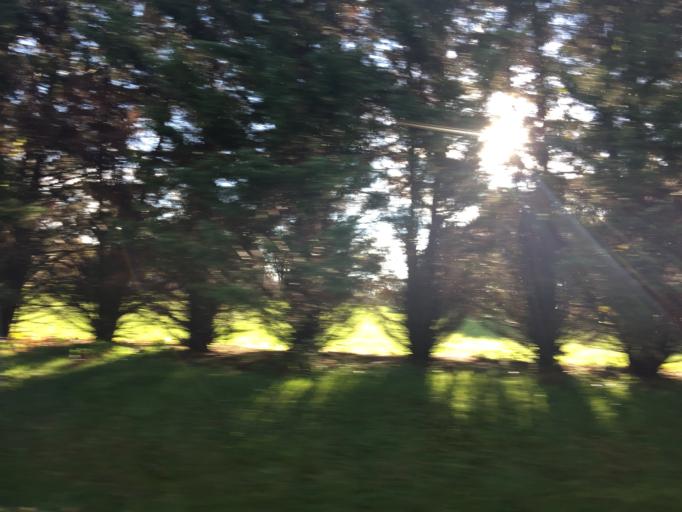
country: US
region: Maryland
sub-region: Howard County
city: Highland
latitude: 39.2657
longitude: -77.0130
